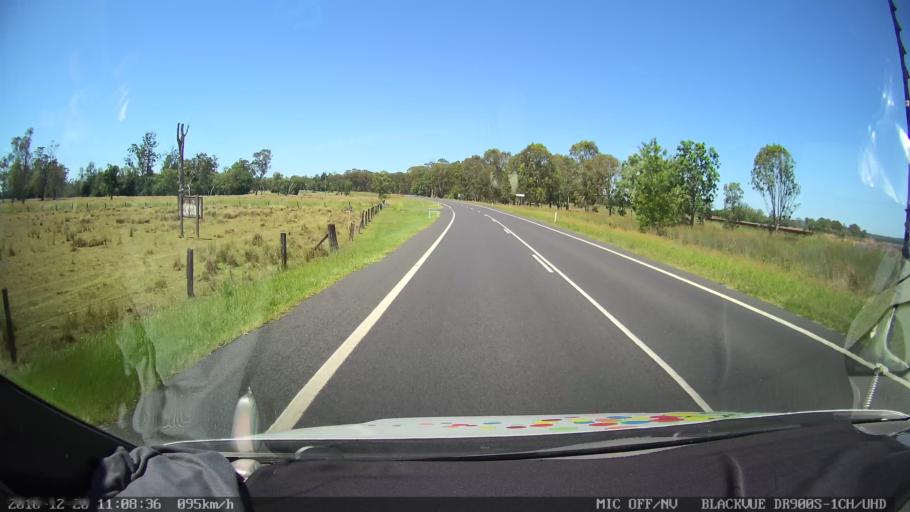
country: AU
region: New South Wales
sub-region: Richmond Valley
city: Casino
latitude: -28.9243
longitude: 153.0054
